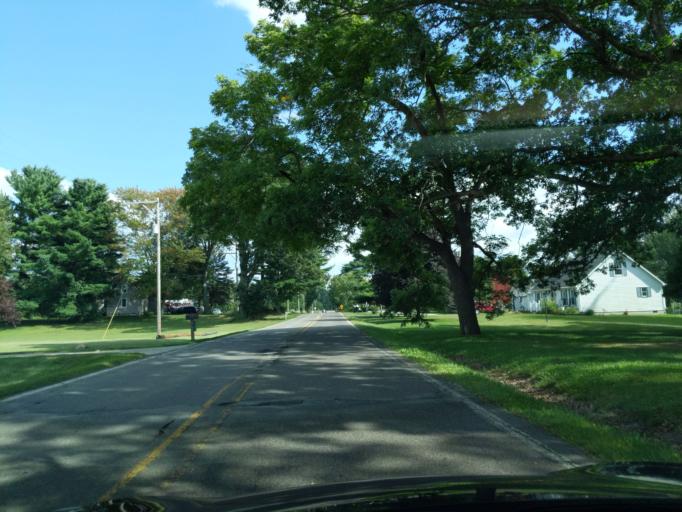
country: US
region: Michigan
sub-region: Jackson County
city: Jackson
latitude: 42.2882
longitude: -84.4669
